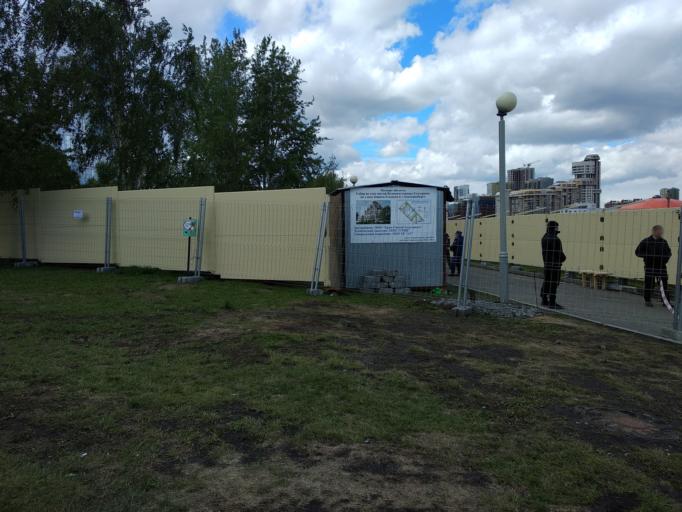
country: RU
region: Sverdlovsk
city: Yekaterinburg
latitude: 56.8414
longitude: 60.5995
